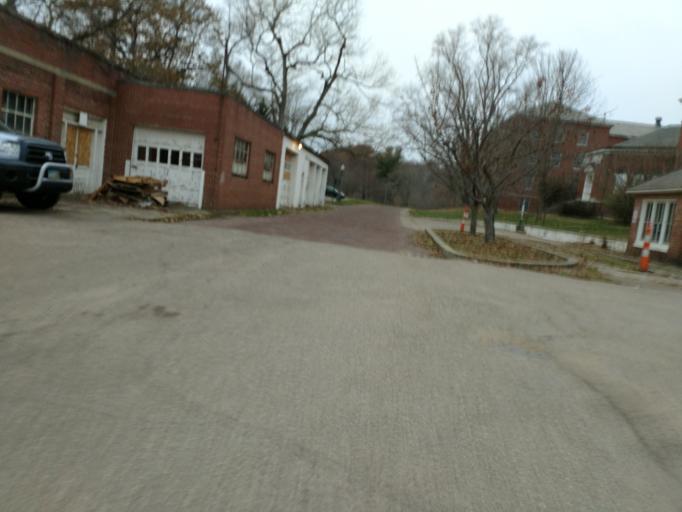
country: US
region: Ohio
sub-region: Athens County
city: Athens
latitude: 39.3195
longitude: -82.1101
